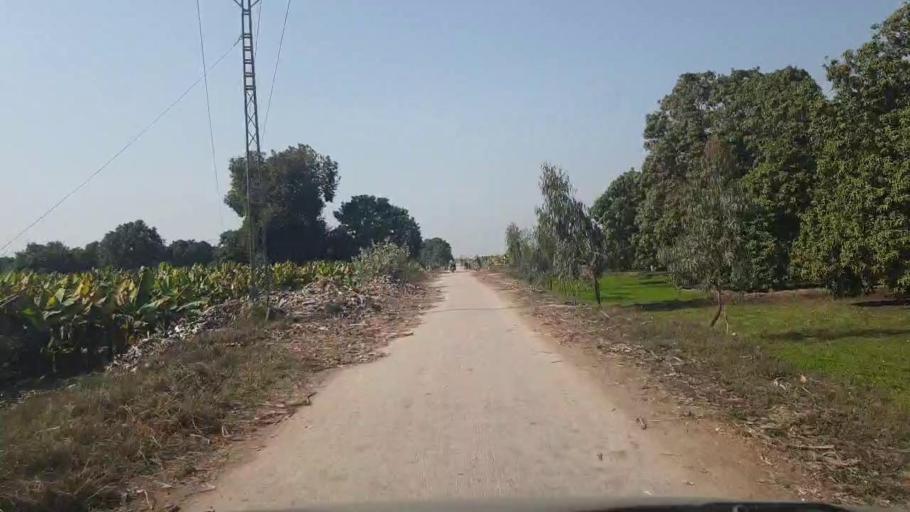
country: PK
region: Sindh
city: Tando Adam
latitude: 25.7694
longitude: 68.6010
